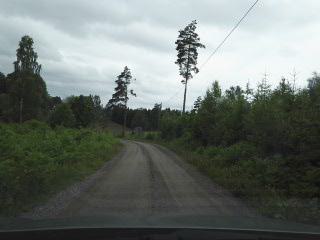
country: SE
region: Joenkoeping
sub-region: Vetlanda Kommun
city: Landsbro
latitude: 57.3221
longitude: 14.8794
